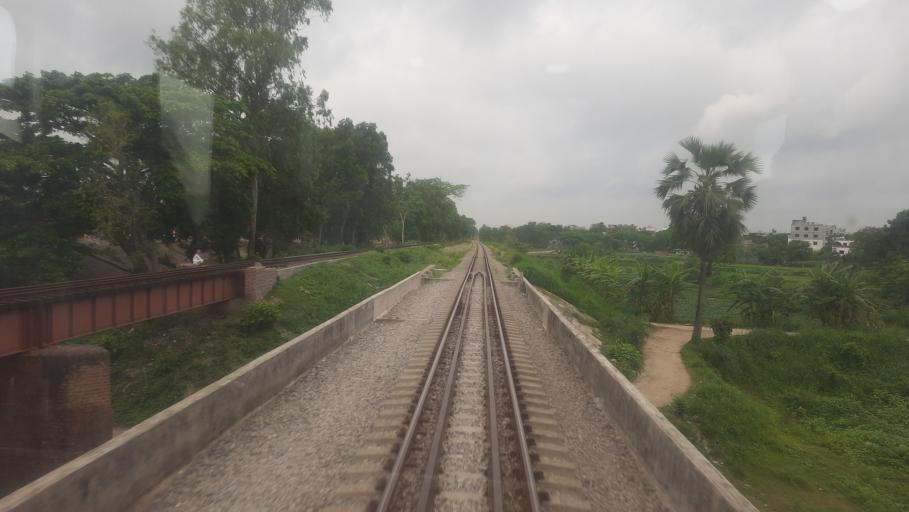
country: BD
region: Dhaka
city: Narsingdi
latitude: 23.9318
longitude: 90.7377
